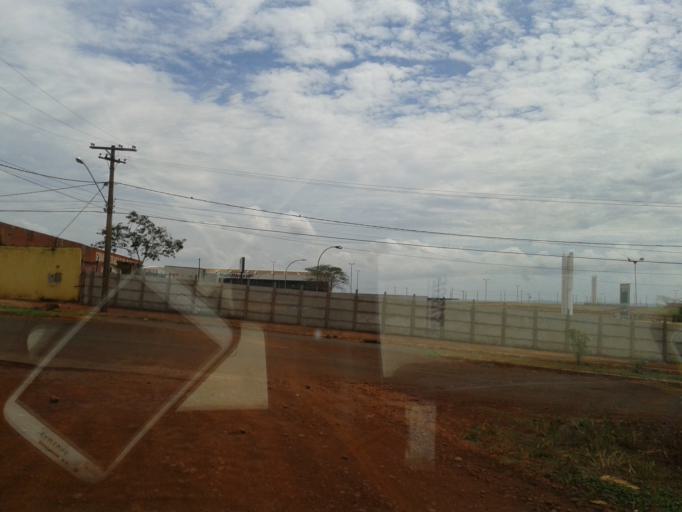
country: BR
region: Goias
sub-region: Itumbiara
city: Itumbiara
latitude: -18.4268
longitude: -49.1912
